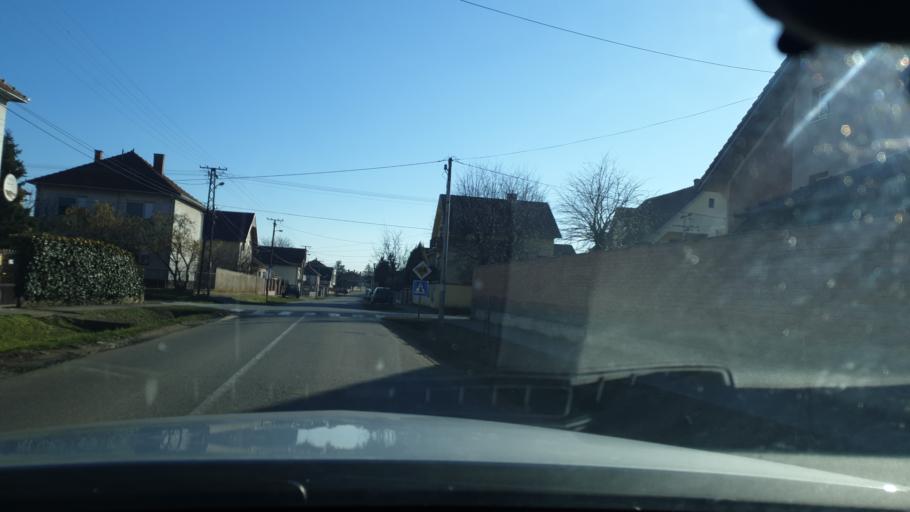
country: RS
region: Autonomna Pokrajina Vojvodina
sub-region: Sremski Okrug
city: Ruma
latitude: 45.0154
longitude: 19.8167
